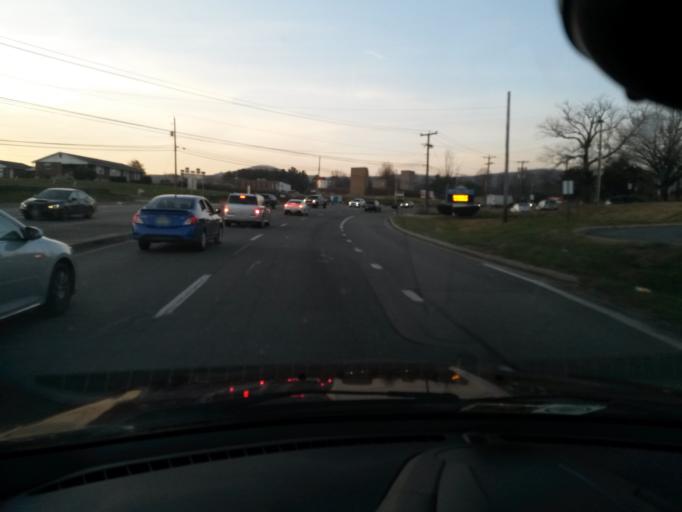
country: US
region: Virginia
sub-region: Roanoke County
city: Hollins
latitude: 37.3503
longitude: -79.9523
